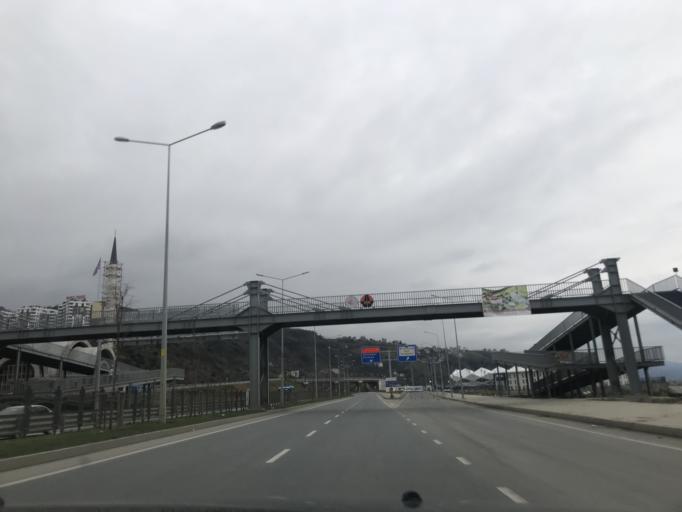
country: TR
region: Trabzon
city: Trabzon
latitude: 40.9959
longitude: 39.6599
